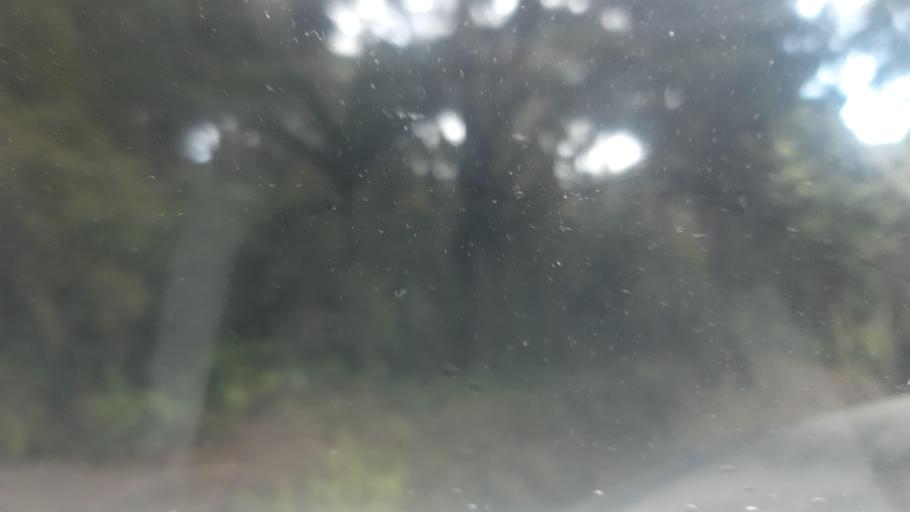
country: NZ
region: Northland
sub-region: Far North District
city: Taipa
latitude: -35.0472
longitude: 173.3927
